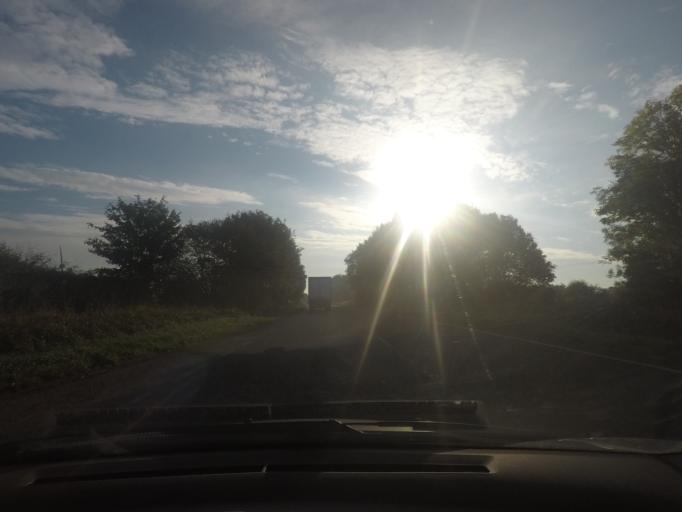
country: GB
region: England
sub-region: East Riding of Yorkshire
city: Hayton
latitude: 53.8898
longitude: -0.7328
